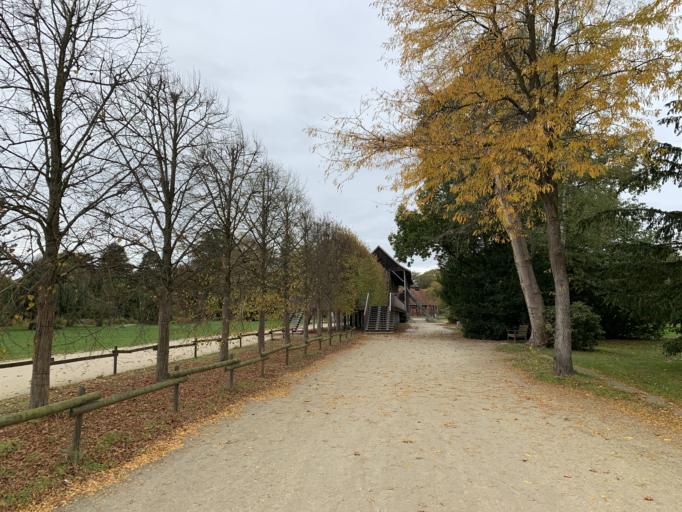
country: DE
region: North Rhine-Westphalia
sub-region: Regierungsbezirk Munster
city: Rheine
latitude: 52.2983
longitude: 7.4226
